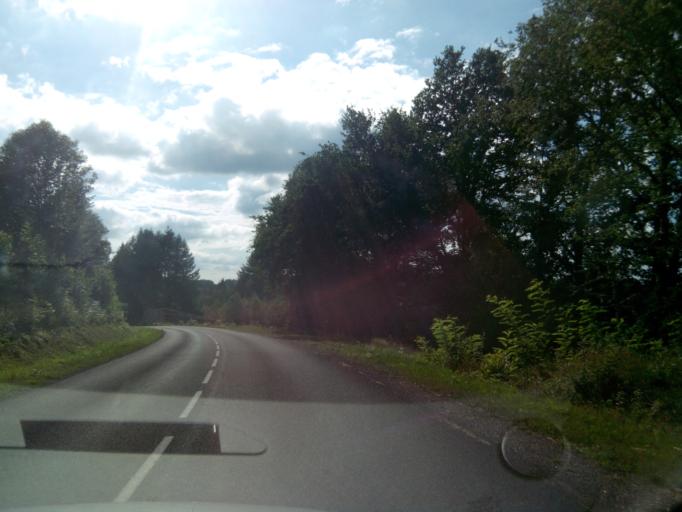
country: FR
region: Limousin
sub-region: Departement de la Haute-Vienne
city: Sauviat-sur-Vige
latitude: 45.8359
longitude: 1.6121
